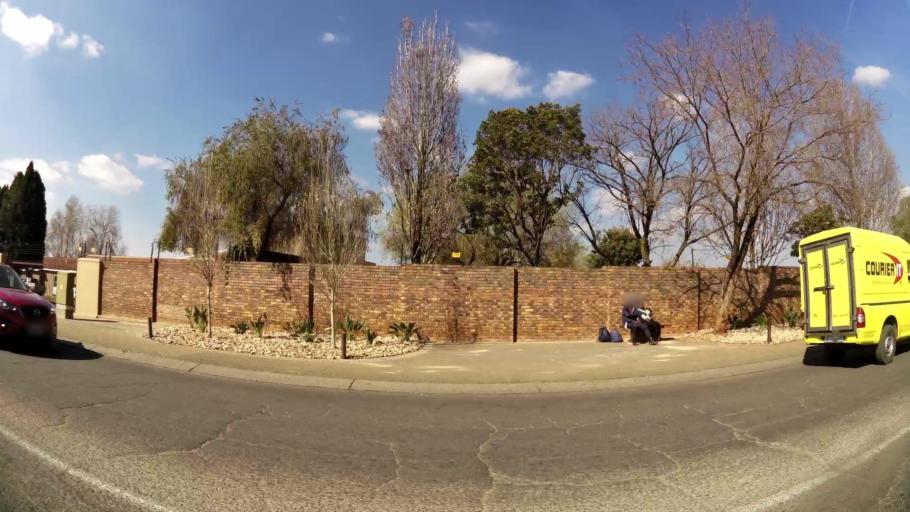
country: ZA
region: Gauteng
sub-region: Ekurhuleni Metropolitan Municipality
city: Tembisa
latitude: -26.0707
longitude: 28.2456
